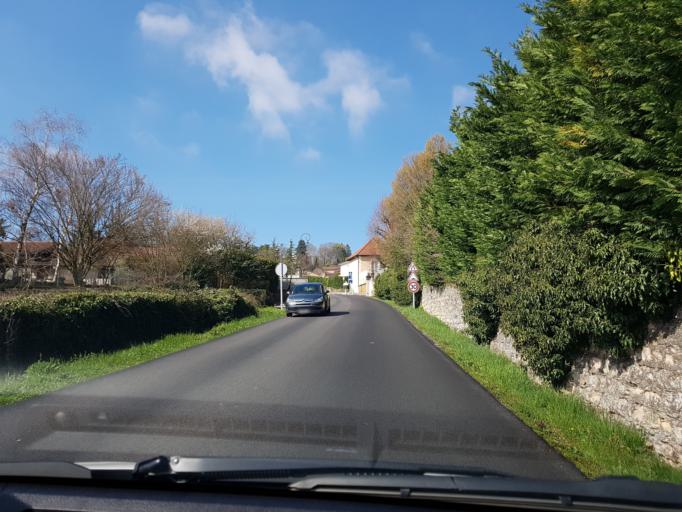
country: FR
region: Rhone-Alpes
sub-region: Departement du Rhone
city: Lucenay
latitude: 45.9276
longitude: 4.6992
